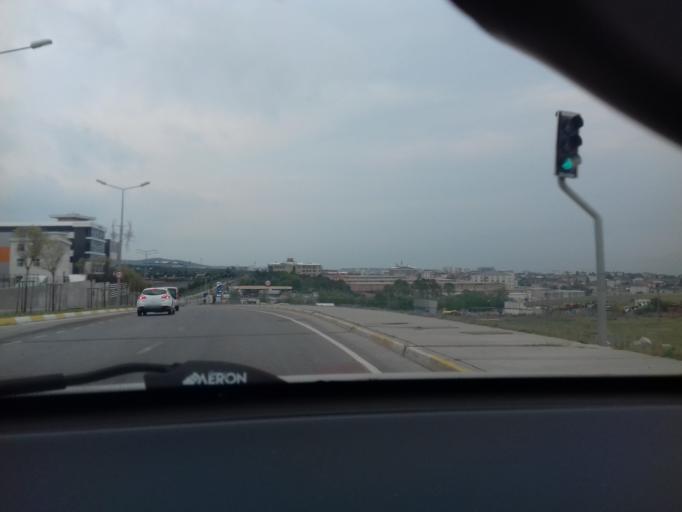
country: TR
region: Istanbul
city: Icmeler
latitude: 40.8862
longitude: 29.3517
